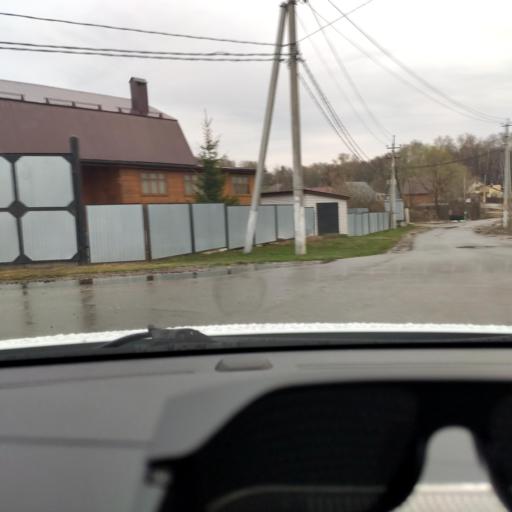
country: RU
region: Tatarstan
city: Vysokaya Gora
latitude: 55.9289
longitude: 49.3050
